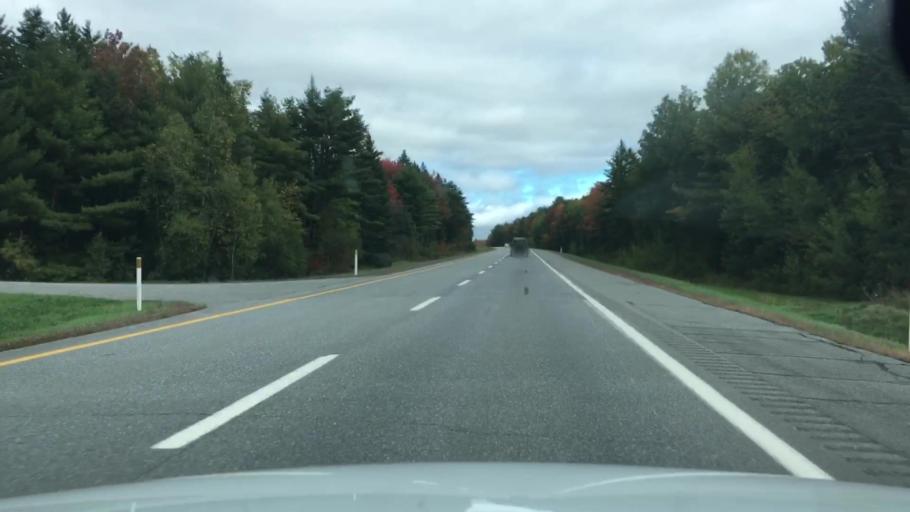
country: US
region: Maine
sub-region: Penobscot County
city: Carmel
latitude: 44.7745
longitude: -69.0370
